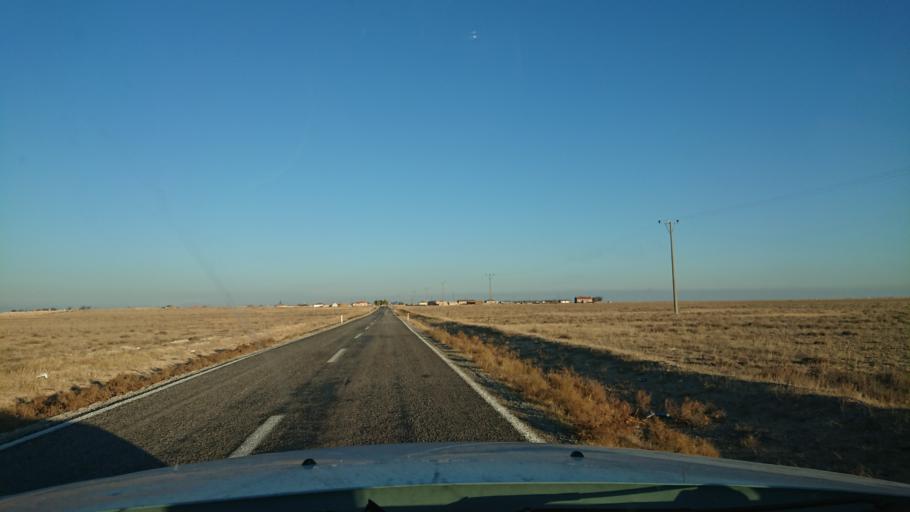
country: TR
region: Aksaray
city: Eskil
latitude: 38.4641
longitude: 33.2399
